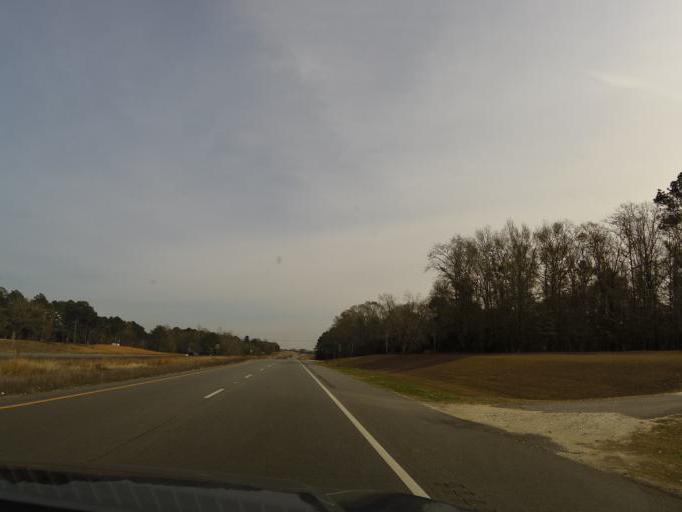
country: US
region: Alabama
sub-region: Houston County
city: Ashford
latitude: 31.1864
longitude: -85.2699
